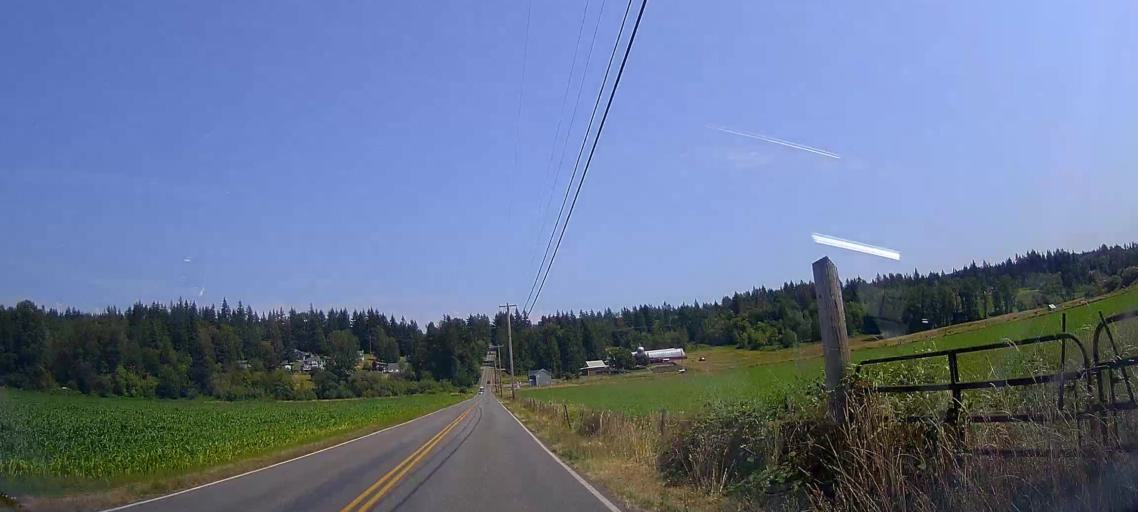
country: US
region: Washington
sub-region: Snohomish County
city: Sisco Heights
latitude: 48.0920
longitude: -122.1349
